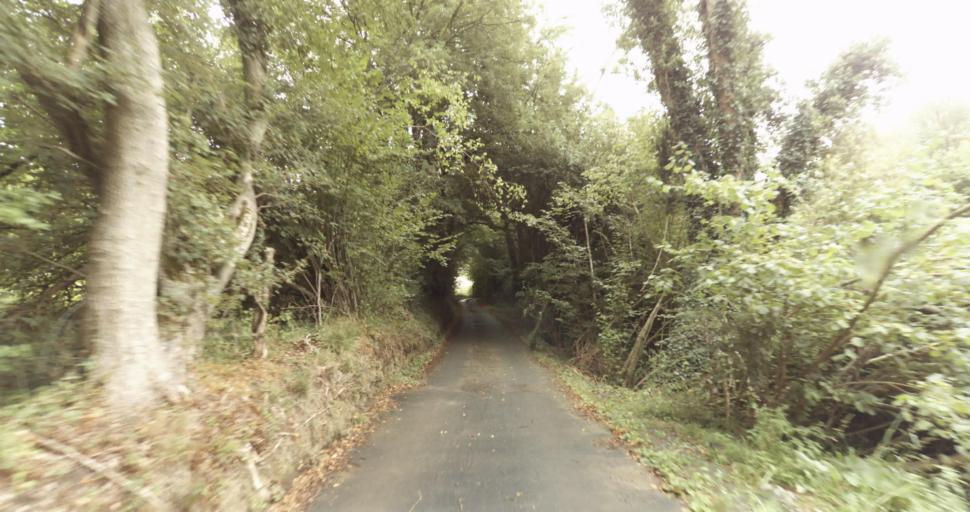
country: FR
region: Lower Normandy
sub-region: Departement de l'Orne
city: Vimoutiers
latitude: 48.9043
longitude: 0.1966
